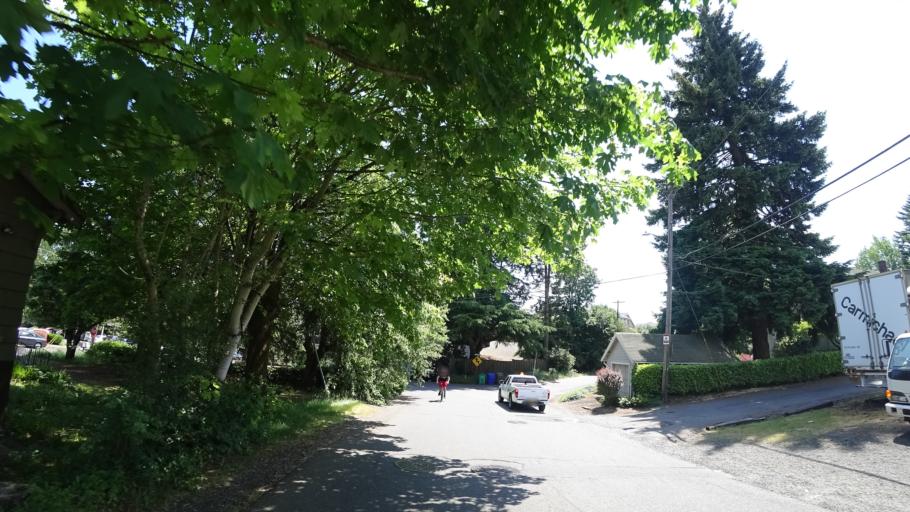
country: US
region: Oregon
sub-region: Clackamas County
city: Lake Oswego
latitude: 45.4653
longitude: -122.7026
